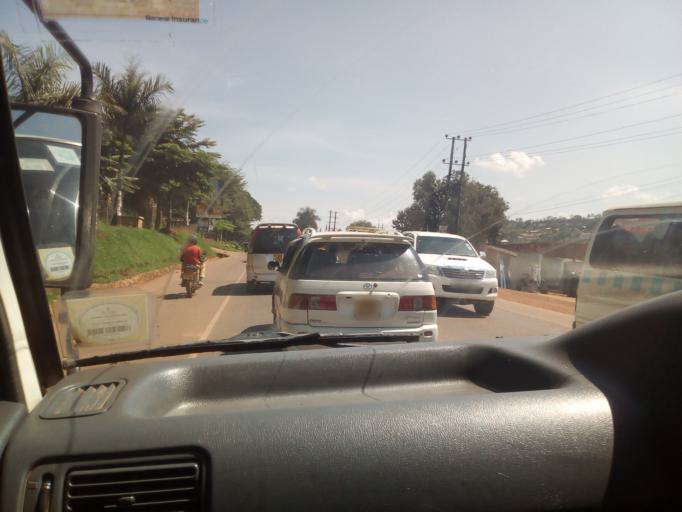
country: UG
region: Central Region
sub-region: Wakiso District
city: Kajansi
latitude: 0.2446
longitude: 32.5576
